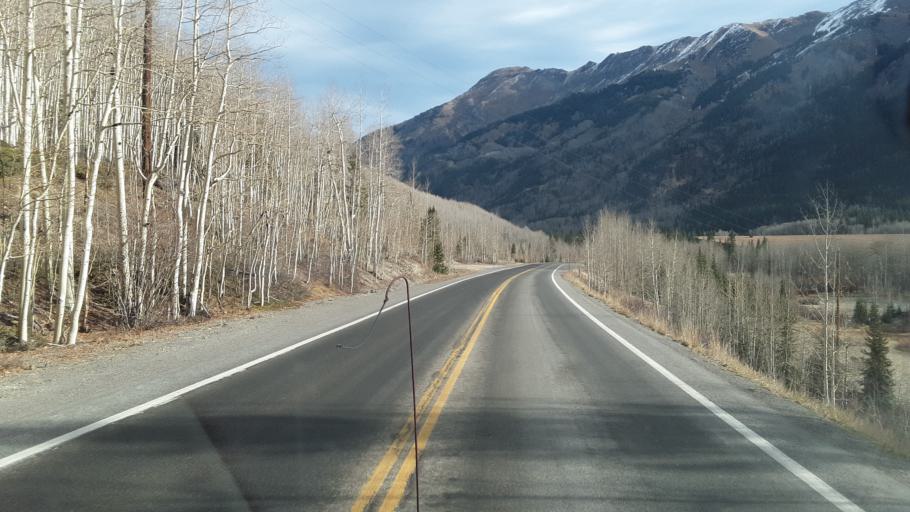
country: US
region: Colorado
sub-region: Ouray County
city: Ouray
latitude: 37.9354
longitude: -107.6809
